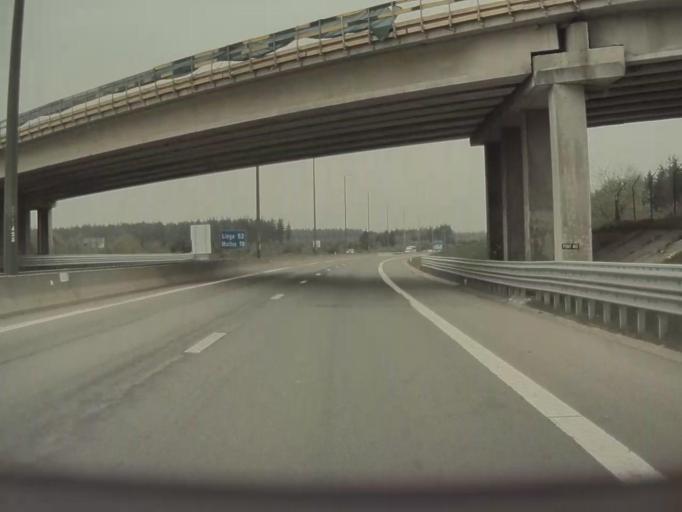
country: BE
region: Wallonia
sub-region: Province du Luxembourg
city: Manhay
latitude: 50.2560
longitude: 5.7260
